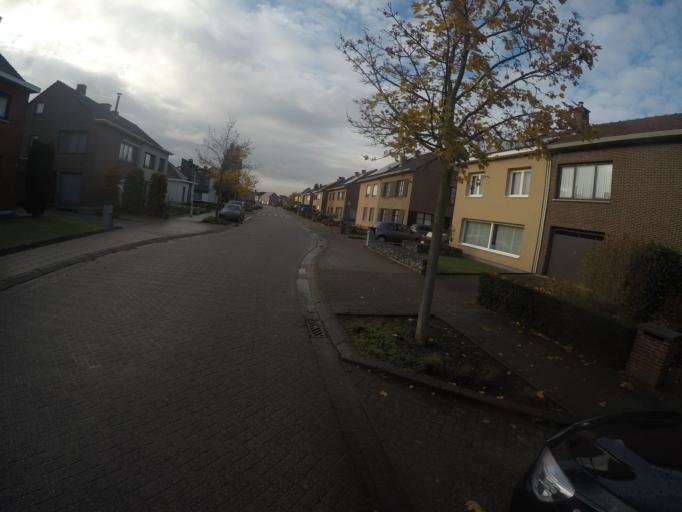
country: BE
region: Flanders
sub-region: Provincie Antwerpen
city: Zwijndrecht
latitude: 51.2089
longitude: 4.3447
